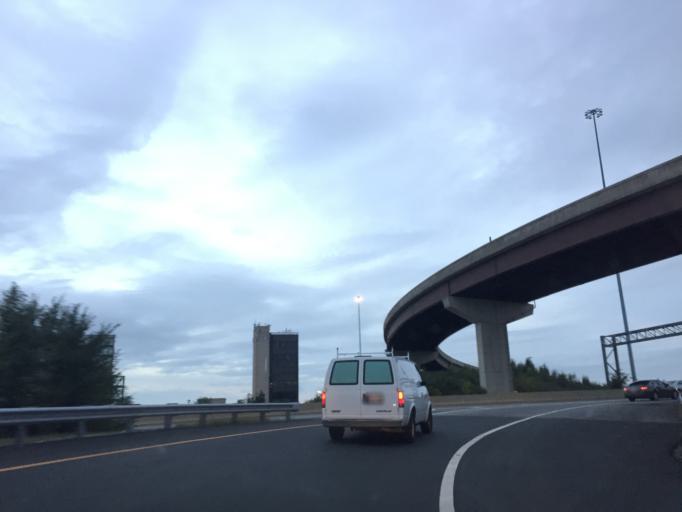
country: US
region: Virginia
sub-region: Fairfax County
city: Springfield
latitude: 38.7784
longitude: -77.1825
